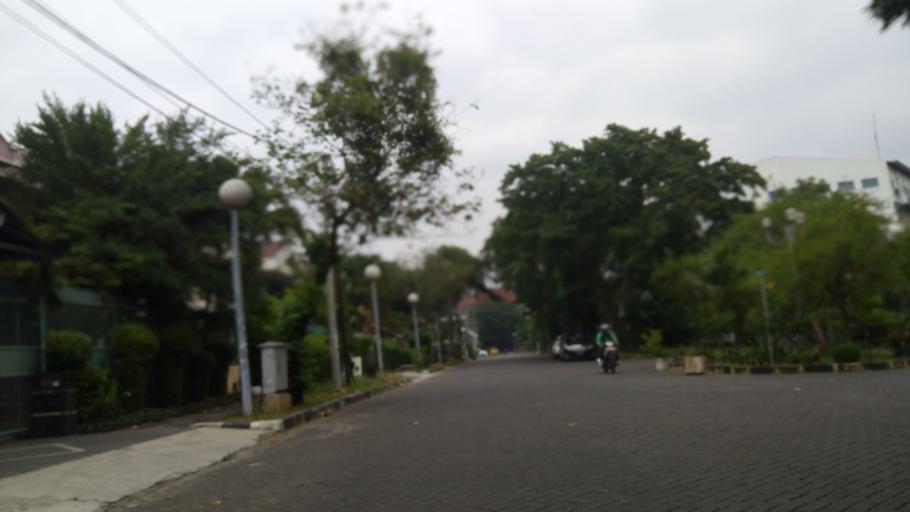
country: ID
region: Jakarta Raya
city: Jakarta
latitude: -6.1528
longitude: 106.8411
